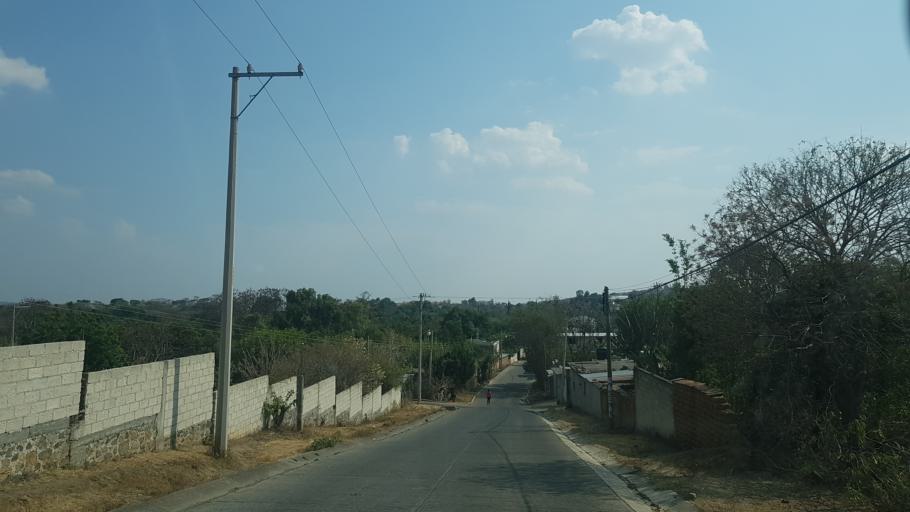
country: MX
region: Puebla
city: San Juan Amecac
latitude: 18.8237
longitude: -98.7044
